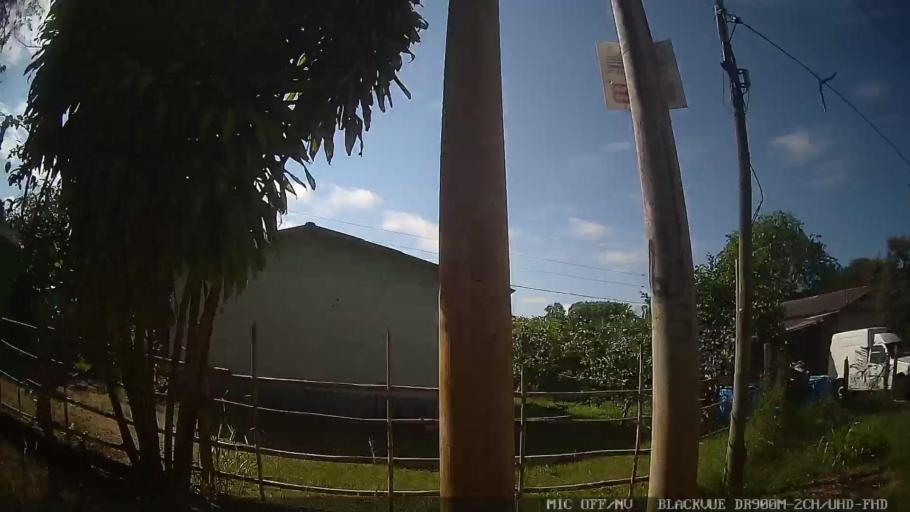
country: BR
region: Sao Paulo
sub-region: Jarinu
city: Jarinu
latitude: -23.0653
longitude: -46.6833
